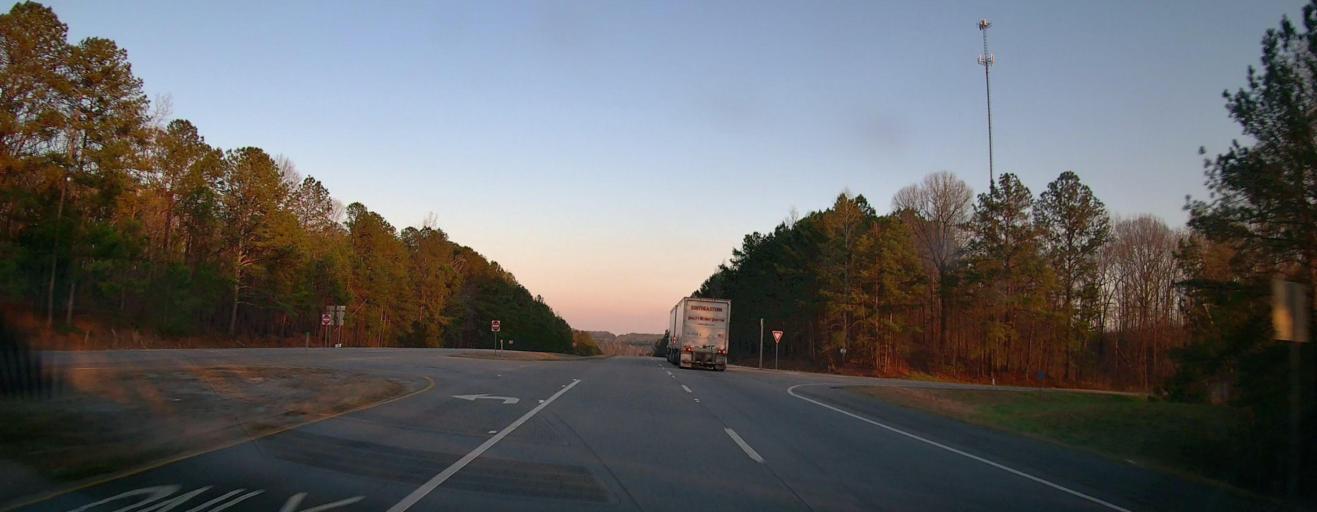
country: US
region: Alabama
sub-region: Coosa County
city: Goodwater
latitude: 33.0433
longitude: -86.1339
